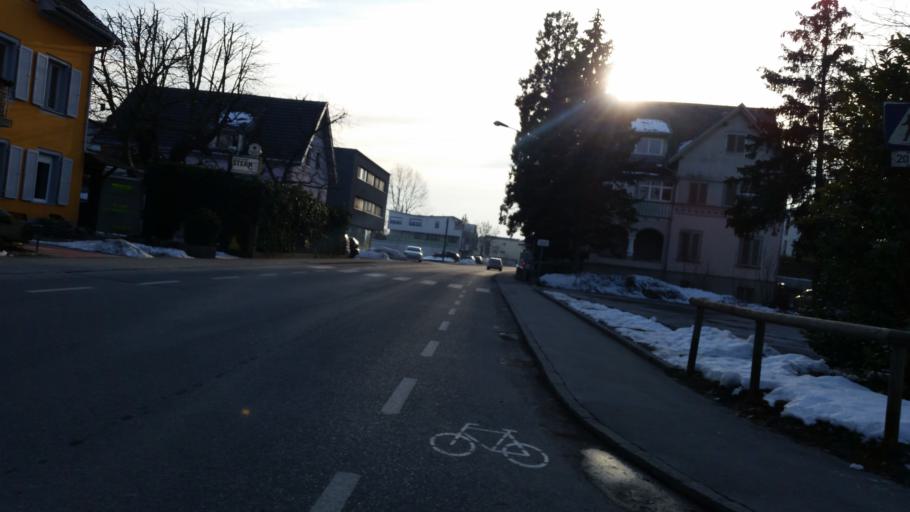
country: AT
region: Vorarlberg
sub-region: Politischer Bezirk Bregenz
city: Hard
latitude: 47.4845
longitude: 9.6869
